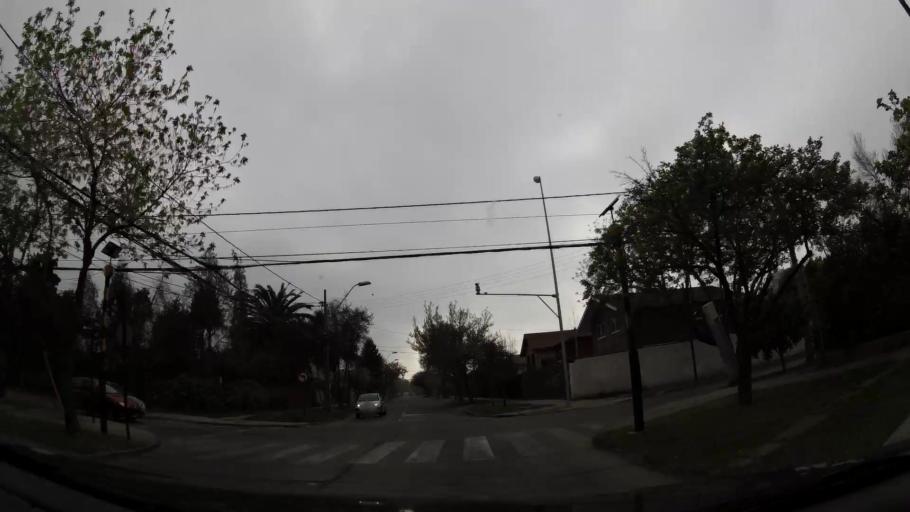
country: CL
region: Santiago Metropolitan
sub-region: Provincia de Santiago
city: Villa Presidente Frei, Nunoa, Santiago, Chile
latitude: -33.3836
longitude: -70.5404
